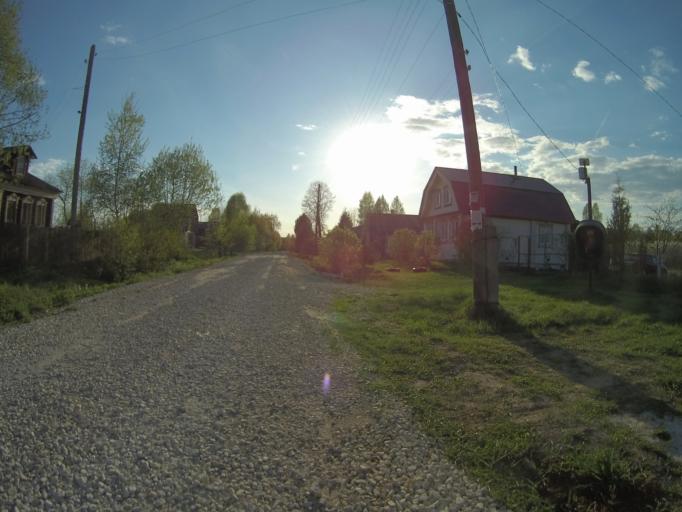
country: RU
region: Vladimir
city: Sudogda
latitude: 56.0758
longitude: 40.7605
